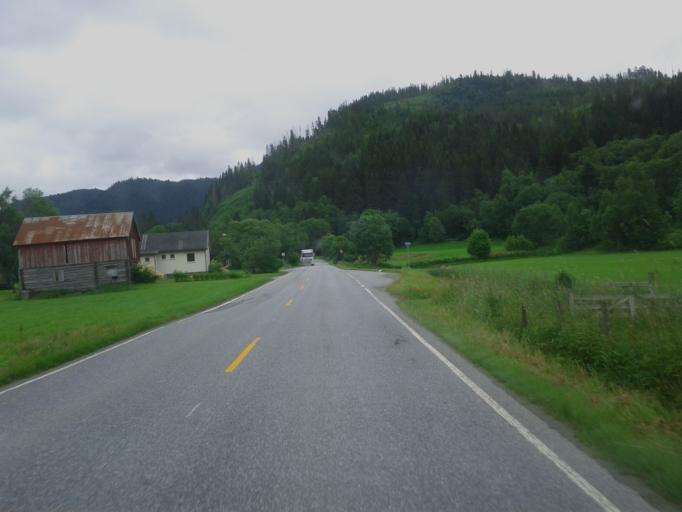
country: NO
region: Sor-Trondelag
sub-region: Midtre Gauldal
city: Storen
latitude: 63.0181
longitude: 10.3342
